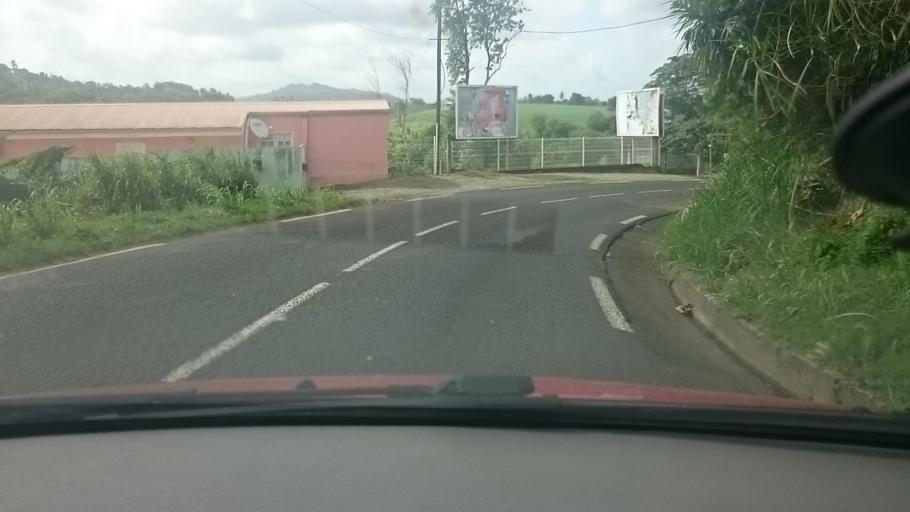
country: MQ
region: Martinique
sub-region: Martinique
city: Saint-Esprit
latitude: 14.5719
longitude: -60.9337
